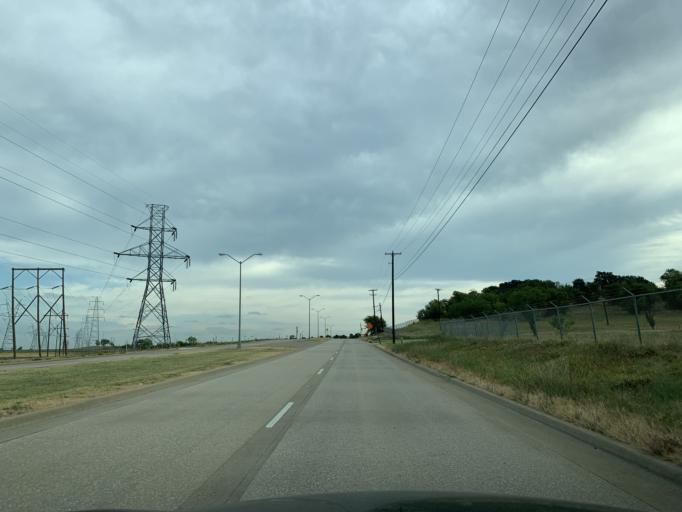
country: US
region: Texas
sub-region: Dallas County
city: Grand Prairie
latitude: 32.7044
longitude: -96.9550
